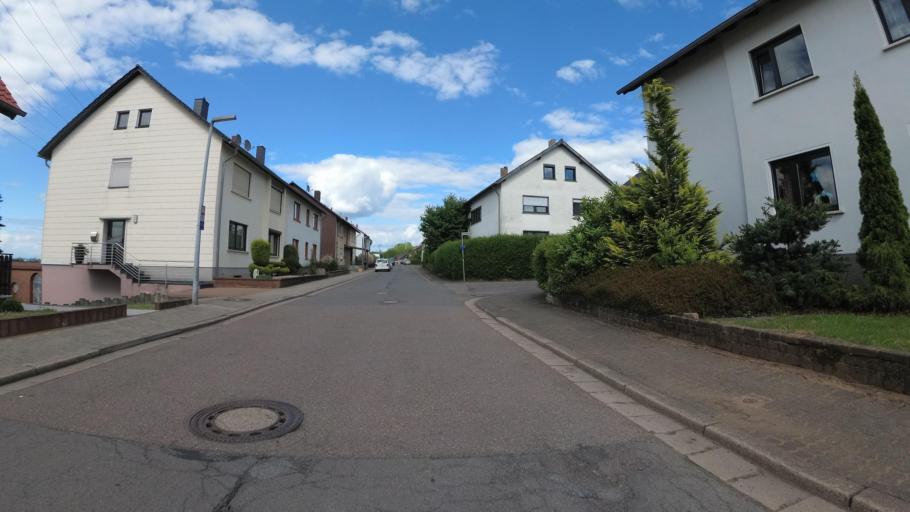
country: DE
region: Saarland
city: Puttlingen
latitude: 49.2931
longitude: 6.9052
